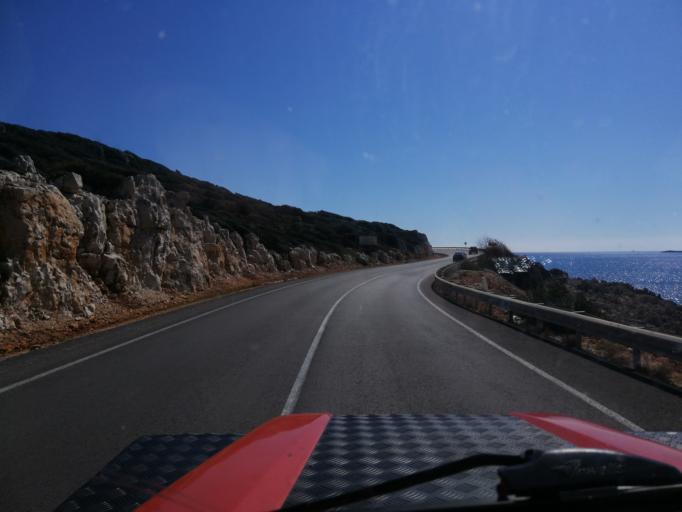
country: GR
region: South Aegean
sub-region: Nomos Dodekanisou
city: Megisti
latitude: 36.2072
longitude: 29.5709
